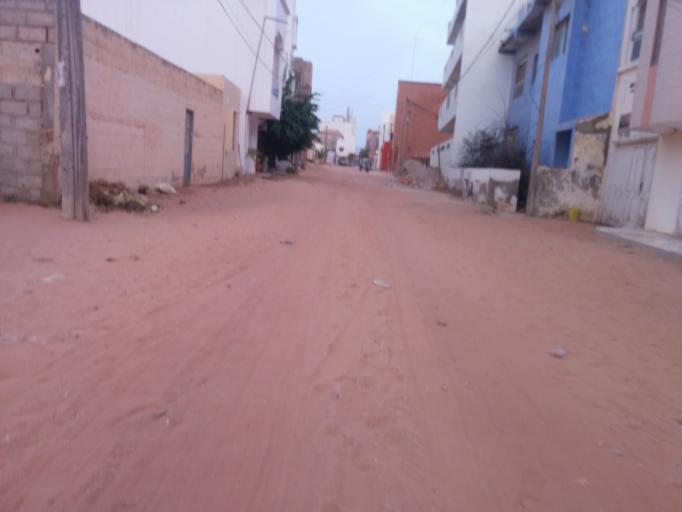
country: SN
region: Dakar
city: Grand Dakar
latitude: 14.7621
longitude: -17.4541
